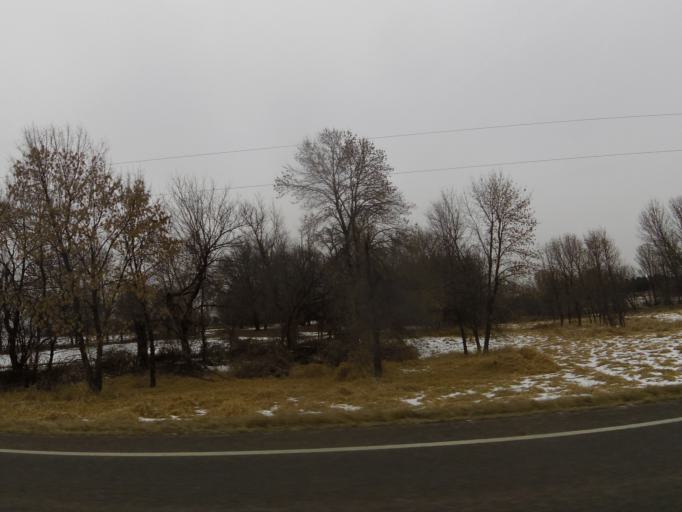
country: US
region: Minnesota
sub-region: Scott County
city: Prior Lake
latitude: 44.6305
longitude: -93.4966
